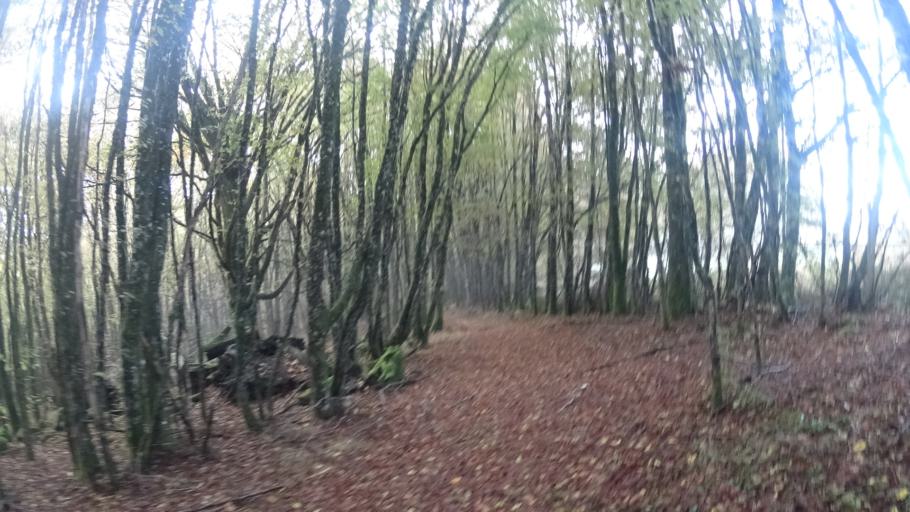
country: FR
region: Aquitaine
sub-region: Departement de la Dordogne
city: Payzac
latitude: 45.3570
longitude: 1.2114
